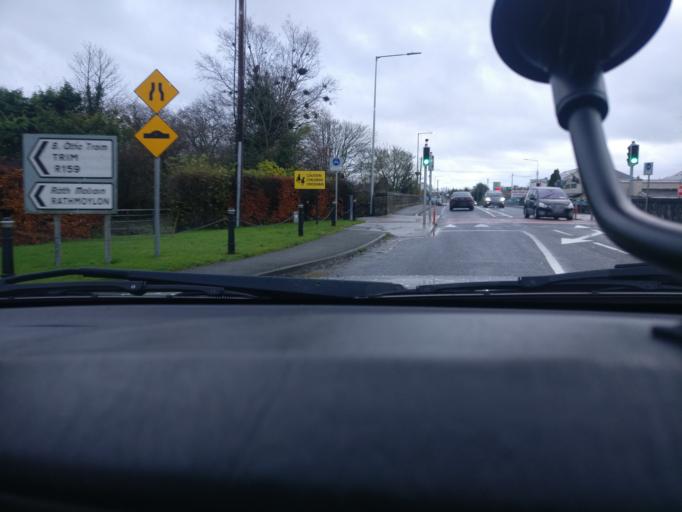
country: IE
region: Leinster
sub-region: An Mhi
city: Enfield
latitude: 53.4157
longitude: -6.8367
